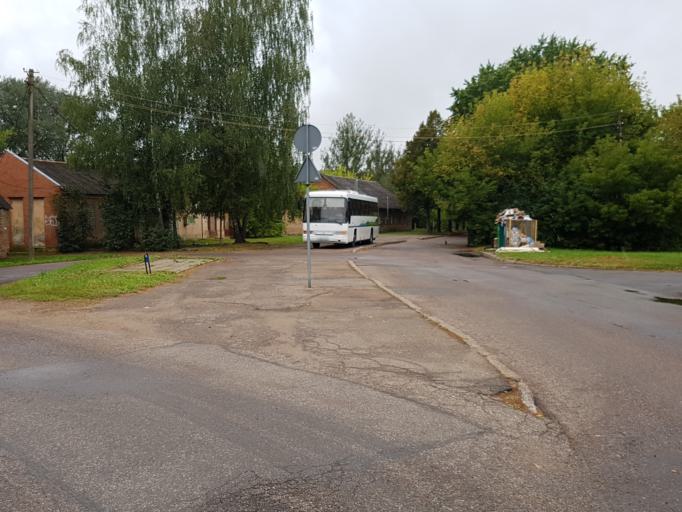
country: LT
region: Vilnius County
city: Lazdynai
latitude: 54.6550
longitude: 25.1955
